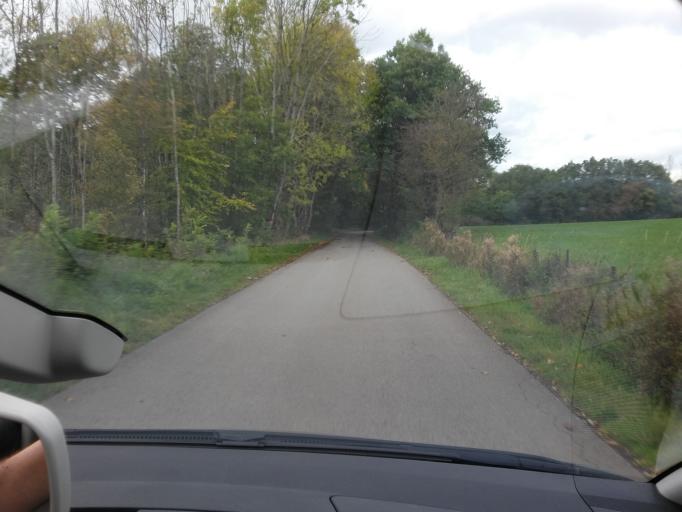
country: BE
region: Wallonia
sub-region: Province du Luxembourg
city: Arlon
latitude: 49.6634
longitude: 5.7643
